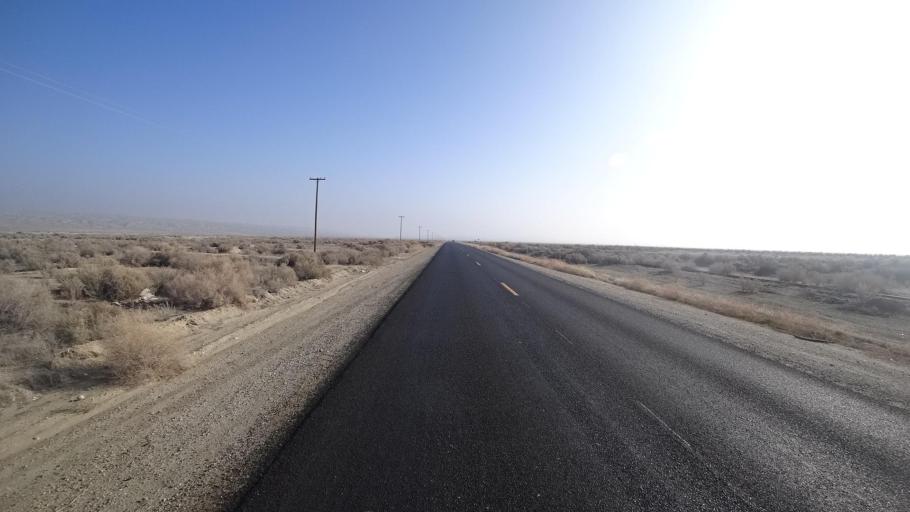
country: US
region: California
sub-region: Kern County
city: Taft Heights
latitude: 35.1805
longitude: -119.5105
